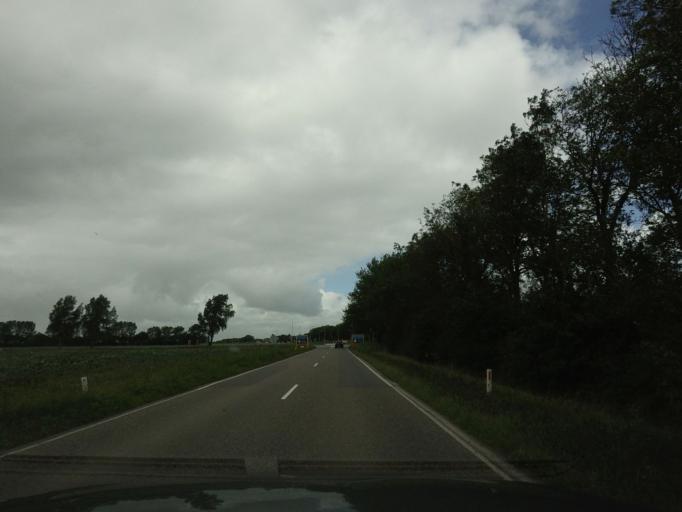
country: NL
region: North Holland
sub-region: Gemeente Langedijk
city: Broek op Langedijk
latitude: 52.7007
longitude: 4.8022
